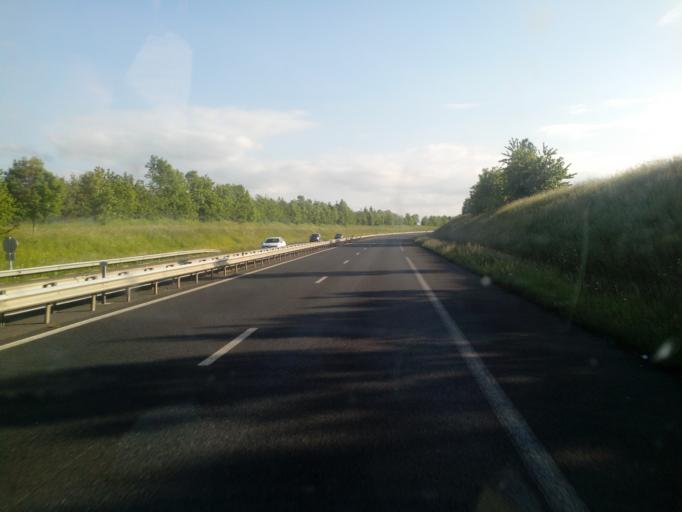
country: FR
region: Lower Normandy
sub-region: Departement du Calvados
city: Grainville-sur-Odon
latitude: 49.1232
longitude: -0.5723
